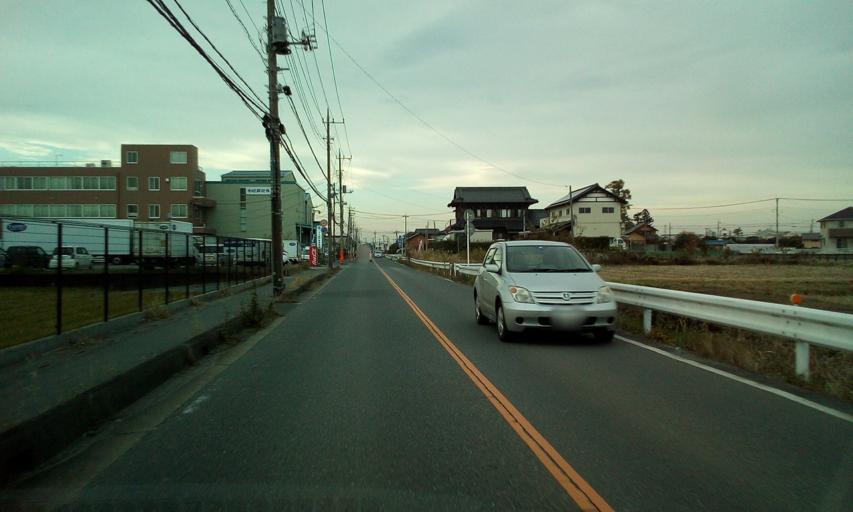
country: JP
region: Saitama
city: Yashio-shi
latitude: 35.8446
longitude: 139.8636
